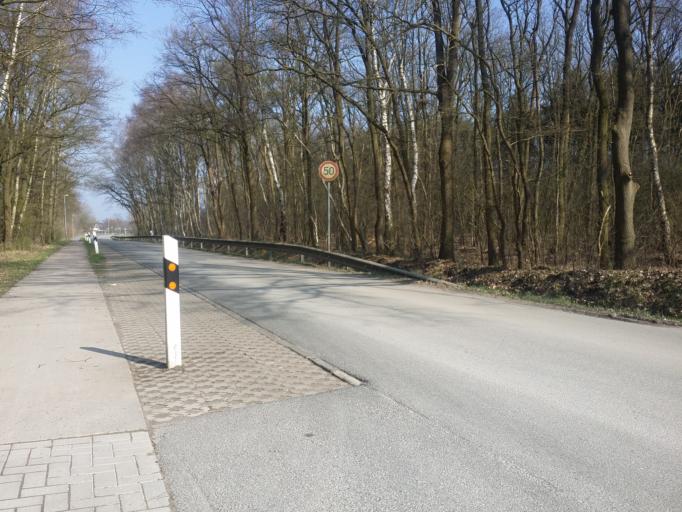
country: DE
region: Lower Saxony
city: Kirchseelte
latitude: 53.0117
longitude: 8.6853
